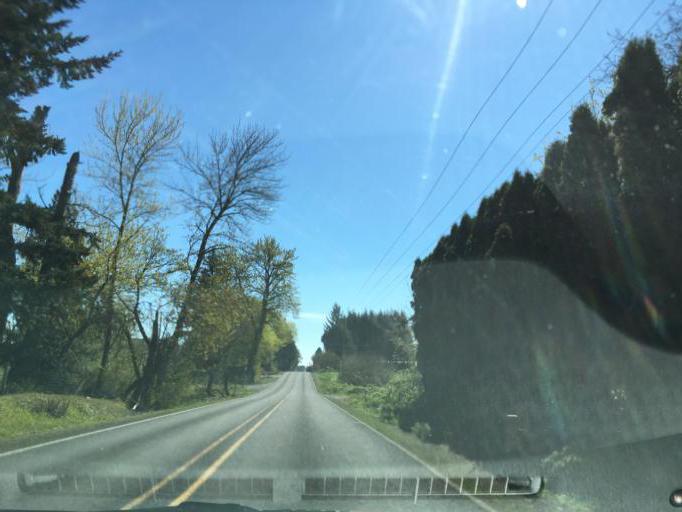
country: US
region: Oregon
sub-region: Clackamas County
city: Canby
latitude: 45.2043
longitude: -122.7228
